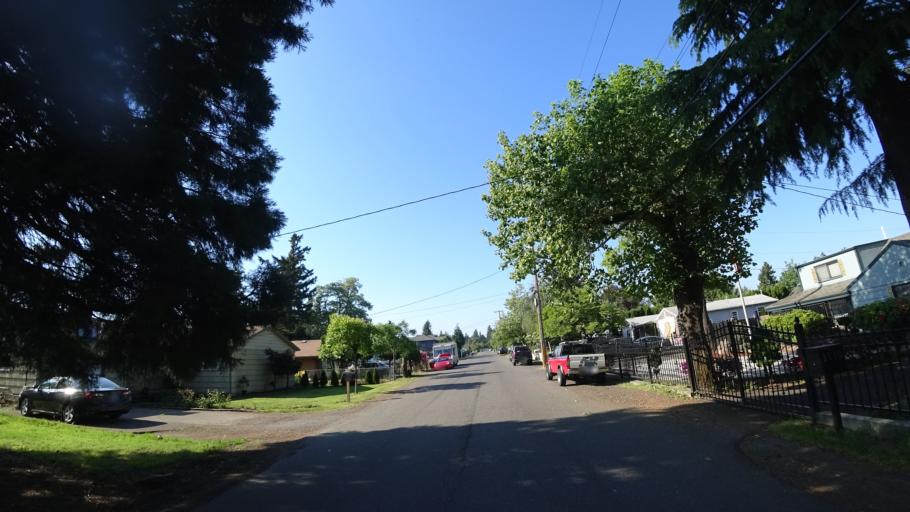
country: US
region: Oregon
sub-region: Multnomah County
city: Lents
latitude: 45.5149
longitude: -122.5081
